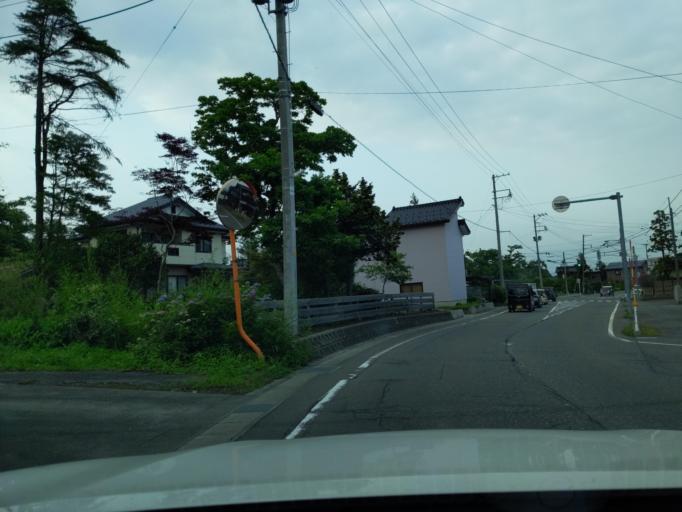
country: JP
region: Niigata
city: Kashiwazaki
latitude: 37.4058
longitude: 138.6005
